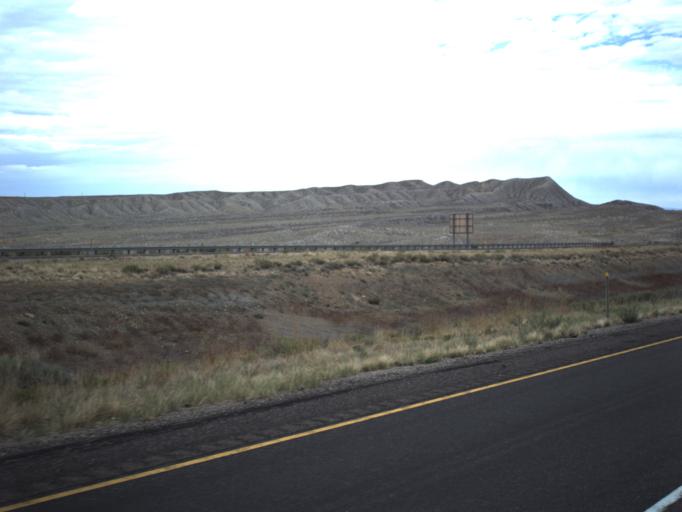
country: US
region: Utah
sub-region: Grand County
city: Moab
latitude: 38.9565
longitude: -109.7082
